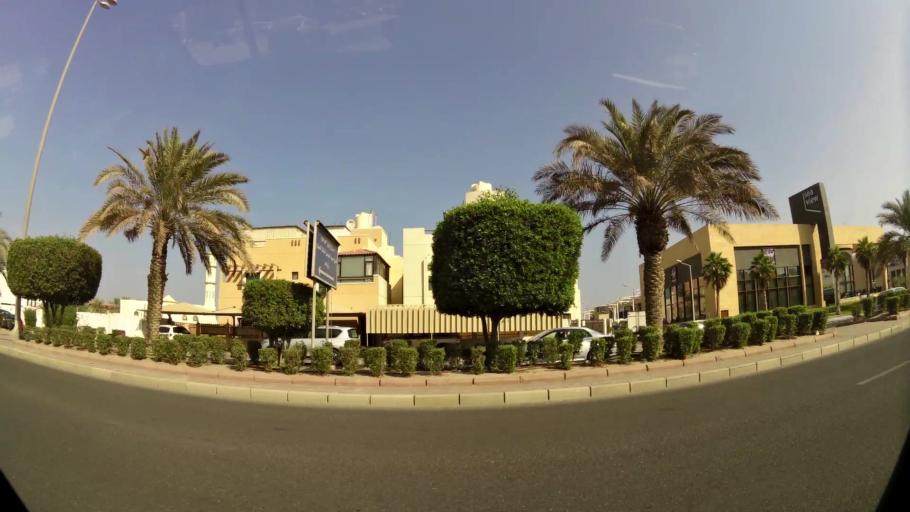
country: KW
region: Al Ahmadi
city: Al Mahbulah
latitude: 29.1366
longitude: 48.1304
